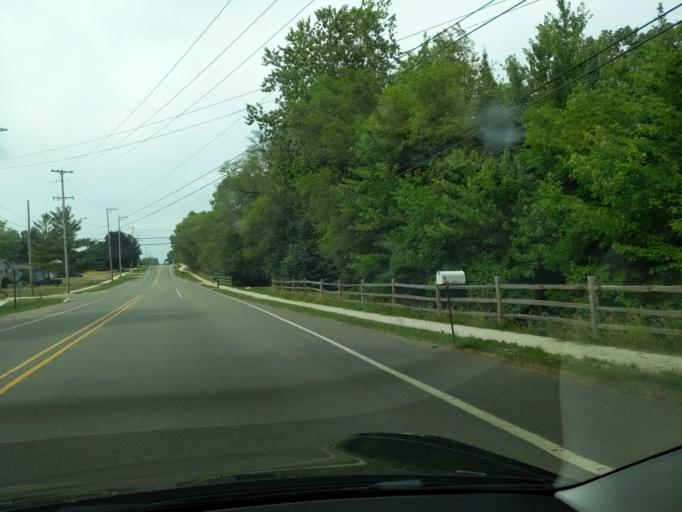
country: US
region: Michigan
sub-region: Clinton County
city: DeWitt
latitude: 42.8250
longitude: -84.6027
